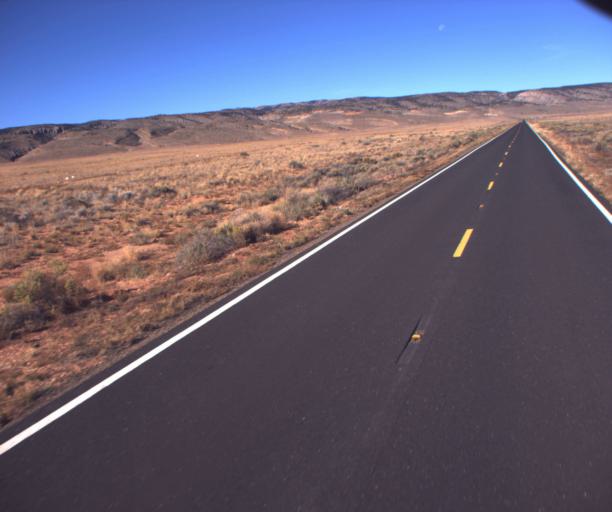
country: US
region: Arizona
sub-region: Coconino County
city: Fredonia
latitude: 36.7233
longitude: -112.0201
